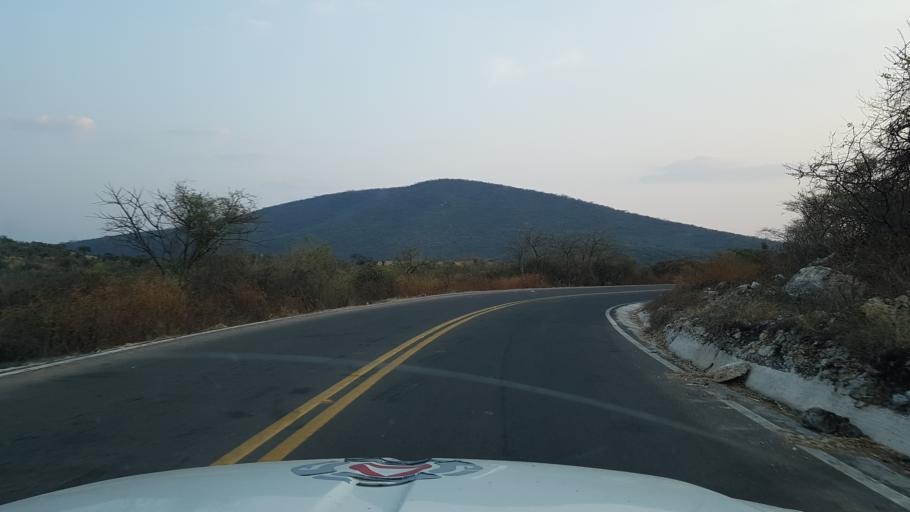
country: MX
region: Morelos
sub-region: Ayala
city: Olintepec
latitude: 18.7318
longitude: -99.0218
